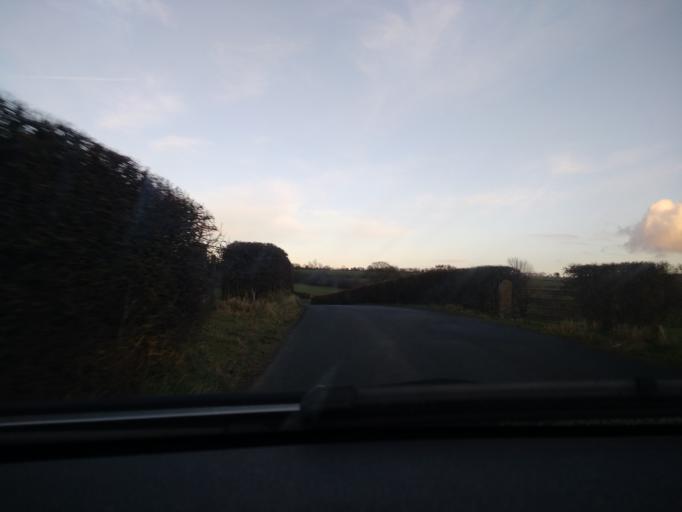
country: GB
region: England
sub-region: Cumbria
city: Carlisle
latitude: 54.7288
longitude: -2.9795
